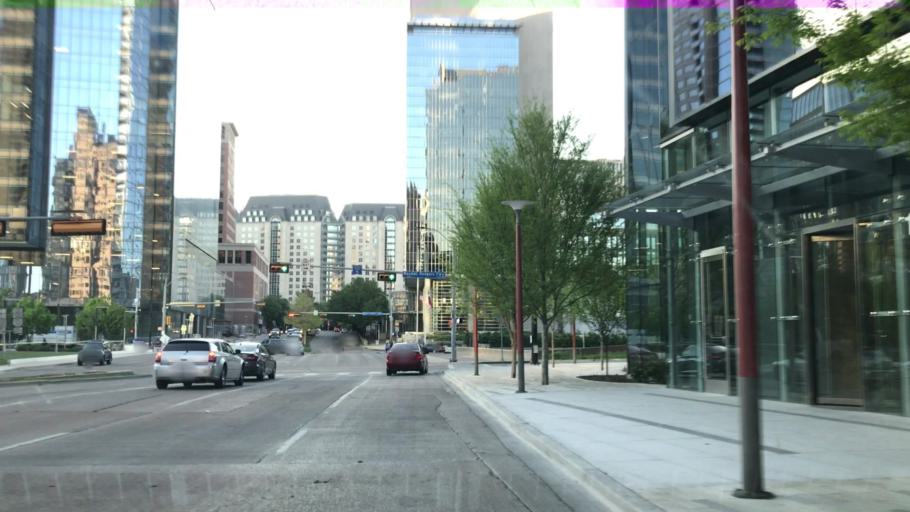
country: US
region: Texas
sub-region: Dallas County
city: Dallas
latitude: 32.7900
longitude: -96.7996
